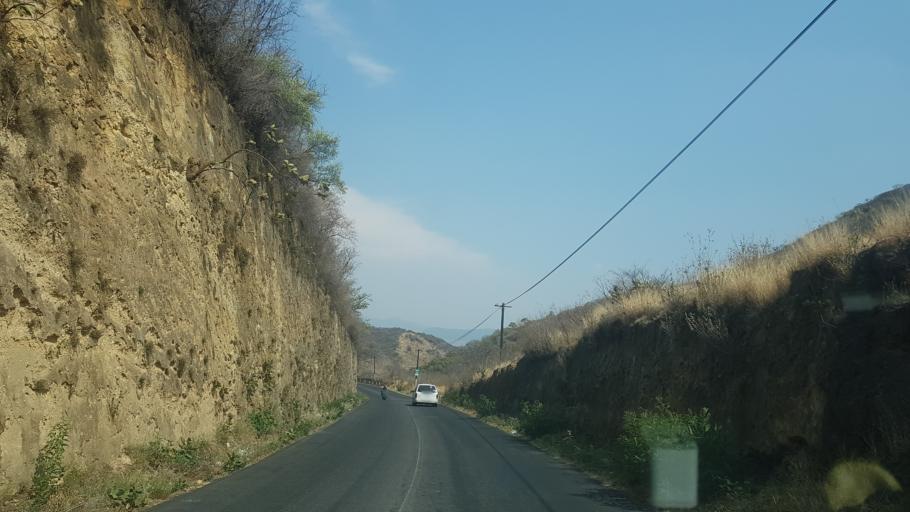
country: MX
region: Puebla
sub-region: Tianguismanalco
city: San Martin Tlapala
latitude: 18.9478
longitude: -98.4594
